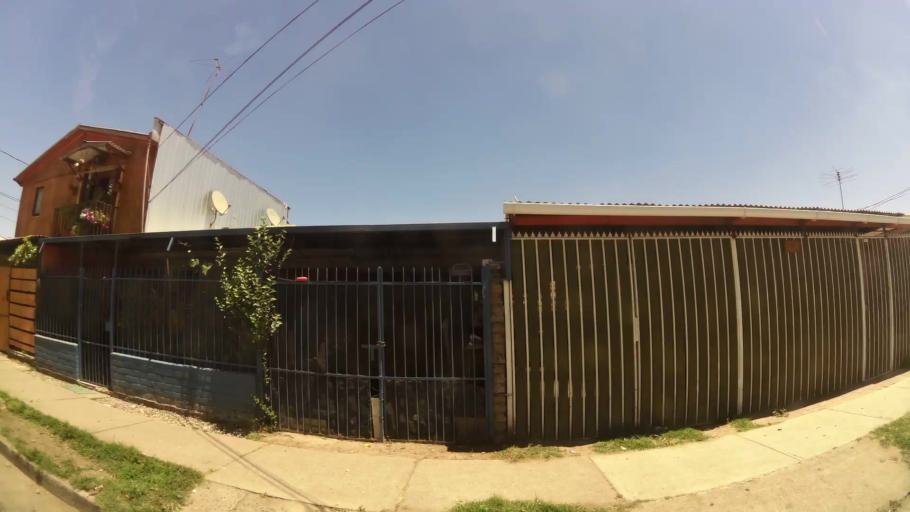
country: CL
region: Santiago Metropolitan
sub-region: Provincia de Santiago
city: La Pintana
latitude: -33.5616
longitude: -70.6428
